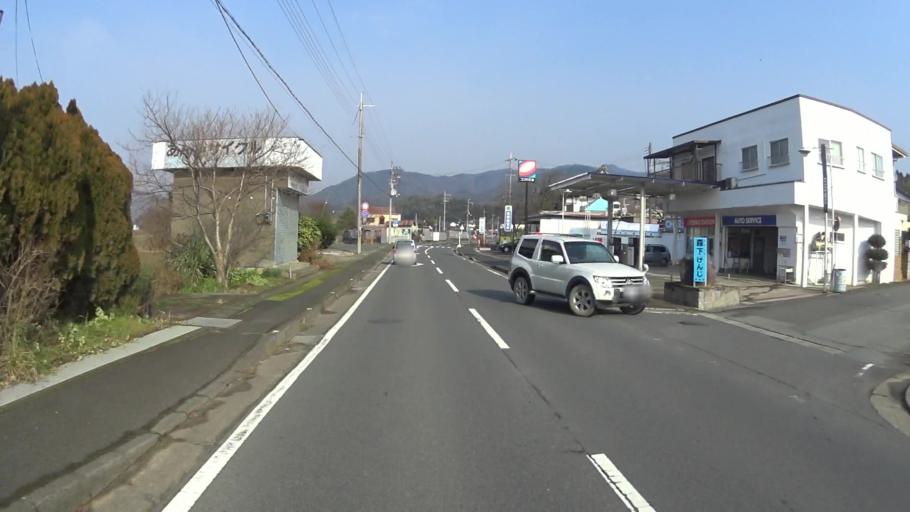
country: JP
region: Kyoto
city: Fukuchiyama
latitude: 35.3077
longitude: 135.1290
